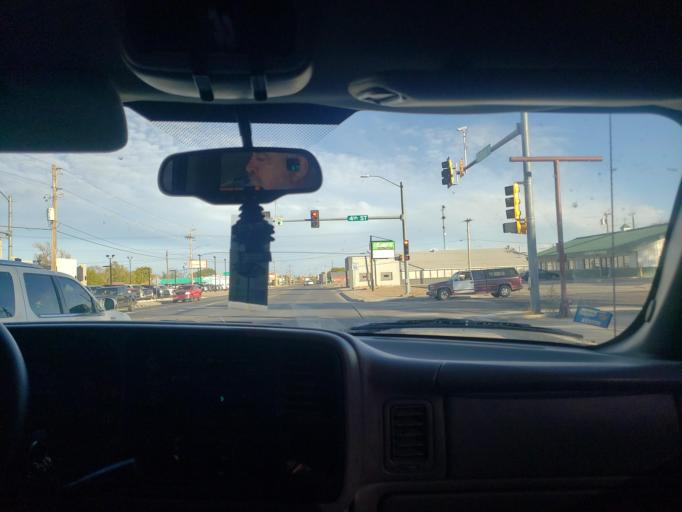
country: US
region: Kansas
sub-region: Finney County
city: Garden City
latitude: 37.9645
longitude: -100.8704
